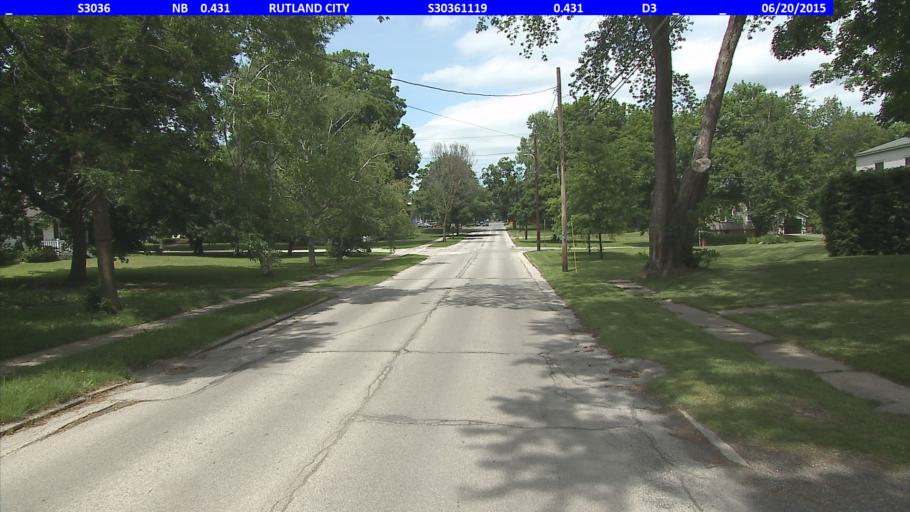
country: US
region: Vermont
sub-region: Rutland County
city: Rutland
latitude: 43.6145
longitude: -72.9767
